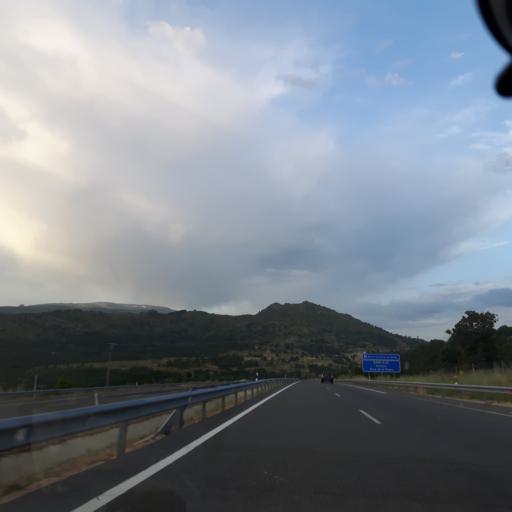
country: ES
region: Castille and Leon
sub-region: Provincia de Salamanca
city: Sorihuela
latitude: 40.4465
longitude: -5.6854
